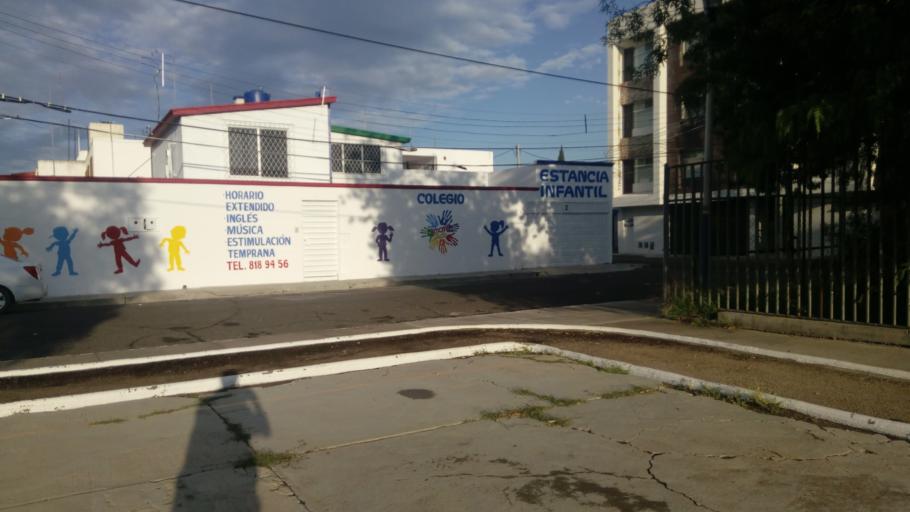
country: MX
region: Durango
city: Victoria de Durango
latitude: 24.0323
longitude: -104.6503
